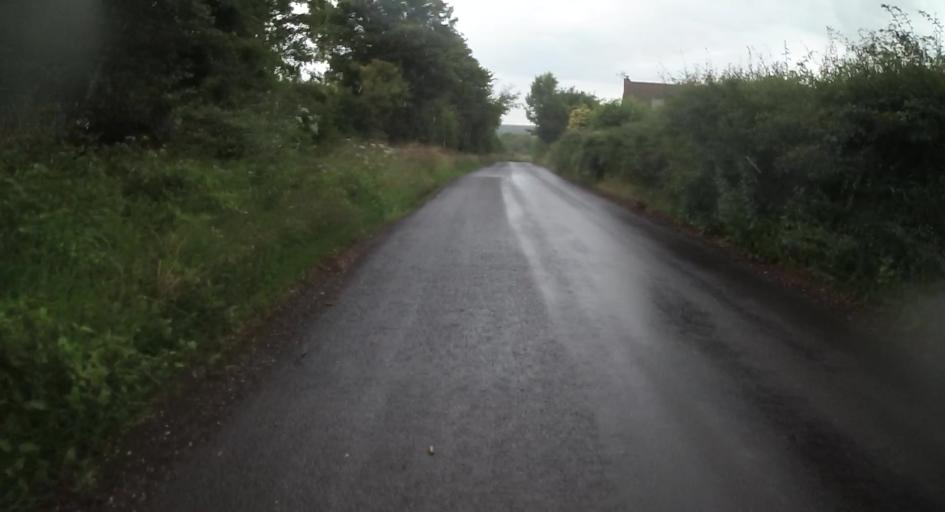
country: GB
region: England
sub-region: Hampshire
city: Odiham
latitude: 51.2507
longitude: -0.9538
